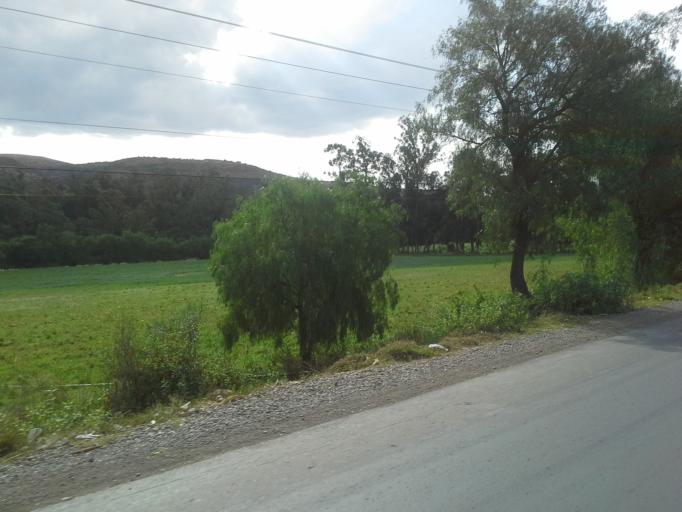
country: BO
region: Cochabamba
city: Cochabamba
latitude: -17.4929
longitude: -66.0932
